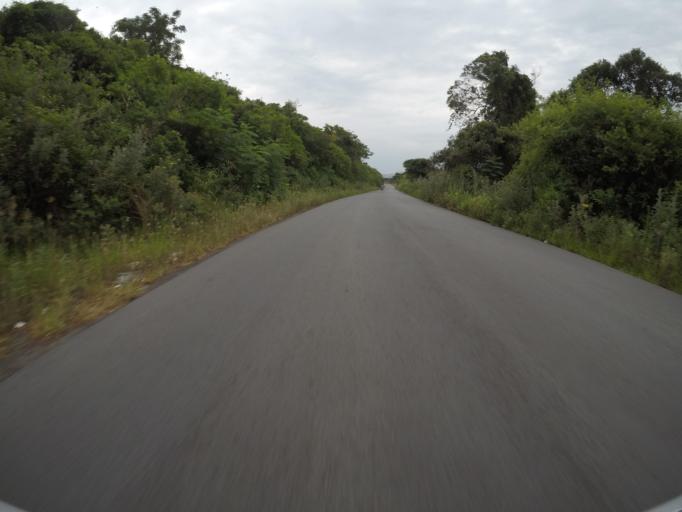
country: ZA
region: Eastern Cape
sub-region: Buffalo City Metropolitan Municipality
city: East London
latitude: -32.9648
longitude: 27.9011
